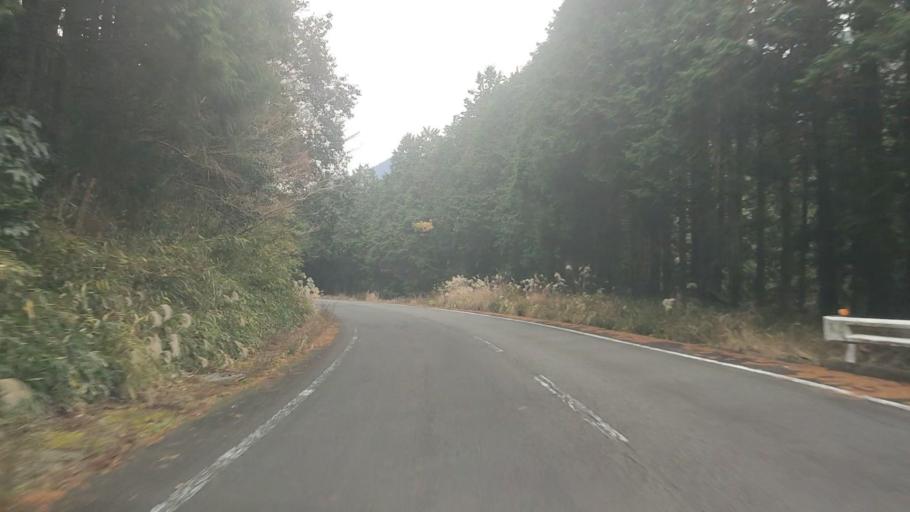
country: JP
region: Nagasaki
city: Shimabara
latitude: 32.7974
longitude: 130.2879
